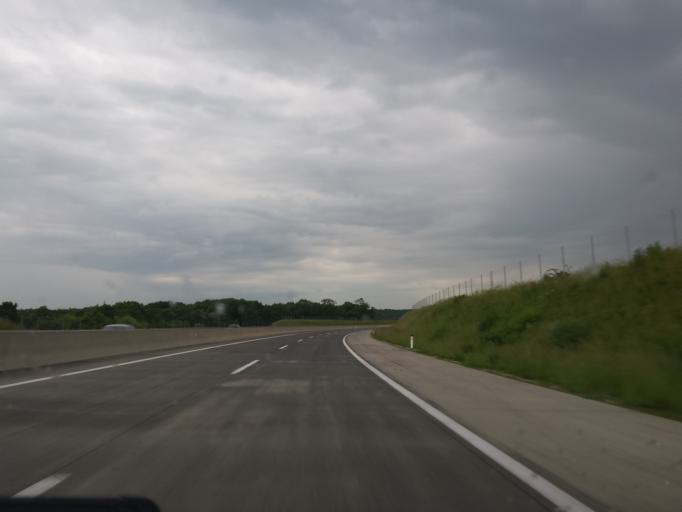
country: AT
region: Lower Austria
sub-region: Politischer Bezirk Mistelbach
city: Hochleithen
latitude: 48.4424
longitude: 16.5567
